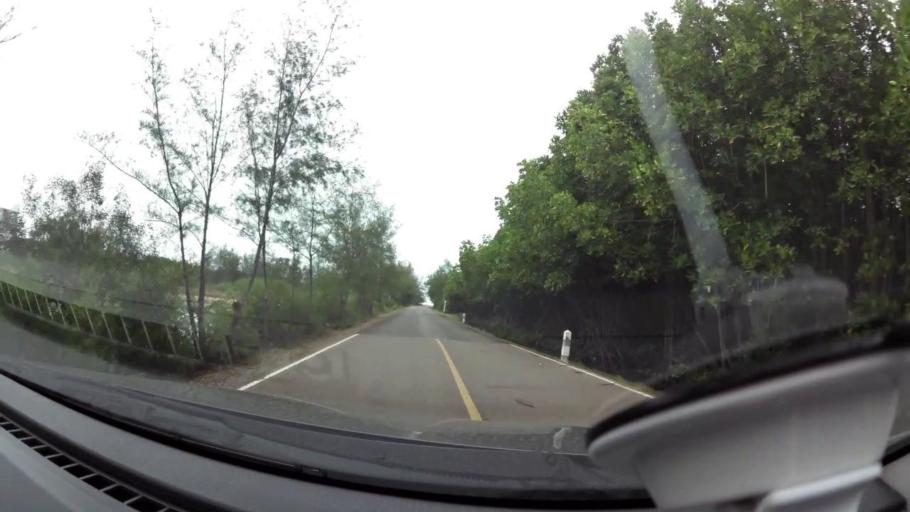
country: TH
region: Prachuap Khiri Khan
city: Pran Buri
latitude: 12.4182
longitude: 99.9810
